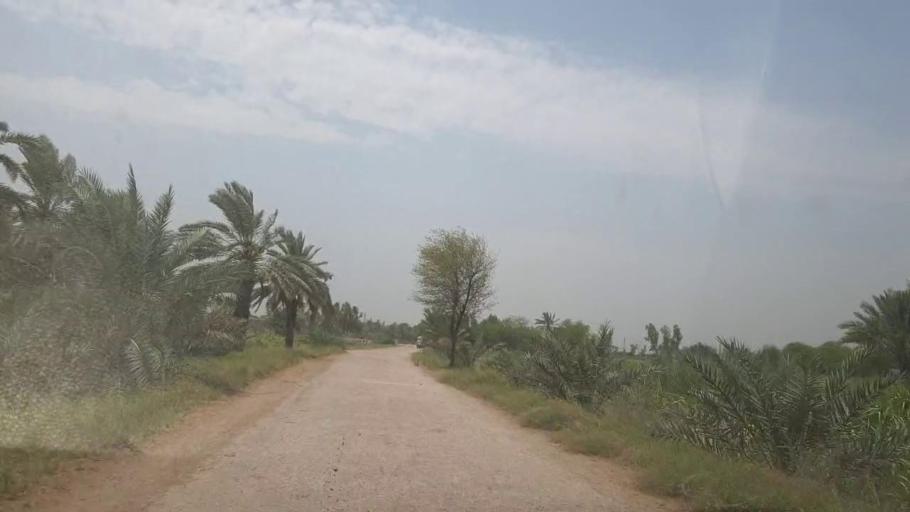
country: PK
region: Sindh
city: Kot Diji
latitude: 27.4423
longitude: 68.6804
